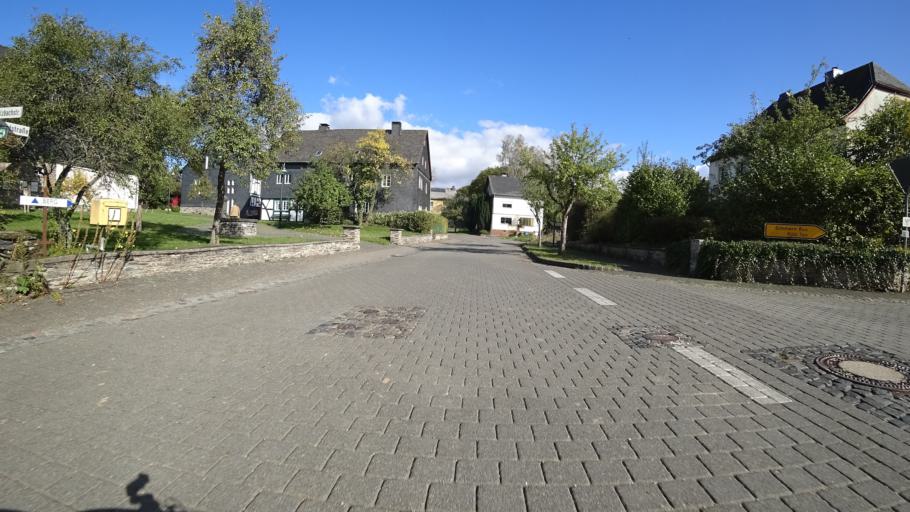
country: DE
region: Rheinland-Pfalz
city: Neuerkirch
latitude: 50.0139
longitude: 7.4908
